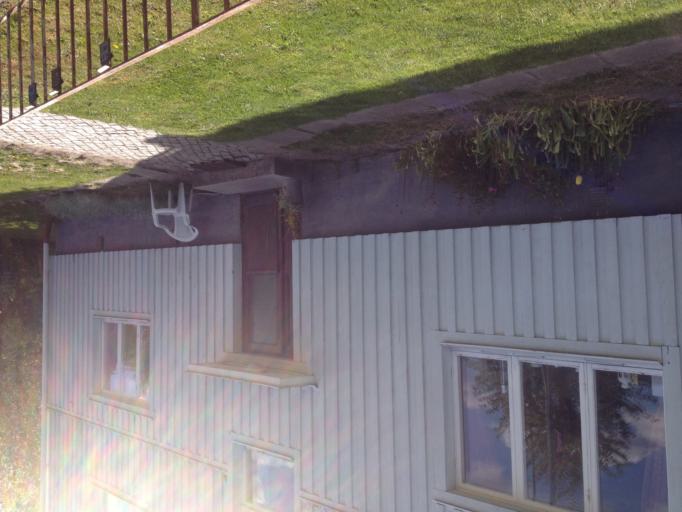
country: SE
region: Blekinge
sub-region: Ronneby Kommun
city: Ronneby
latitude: 56.2052
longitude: 15.2881
